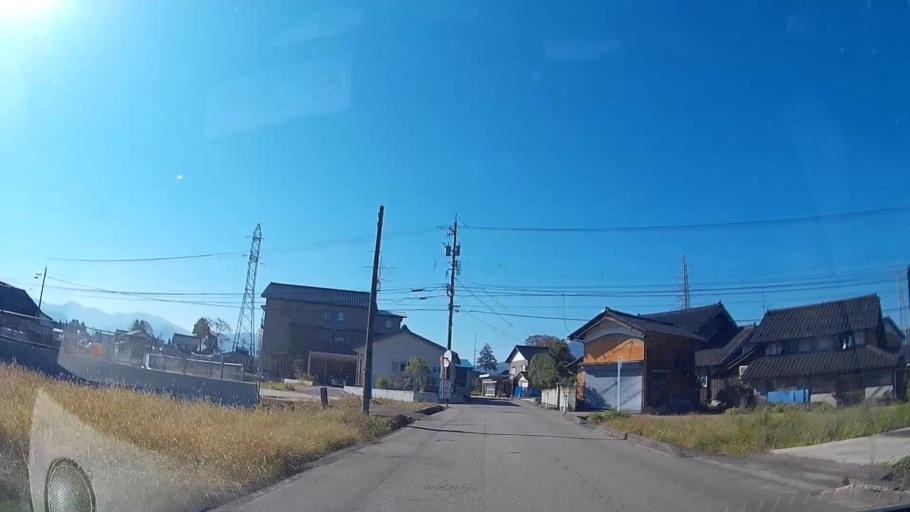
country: JP
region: Toyama
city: Fukumitsu
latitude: 36.5500
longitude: 136.8745
